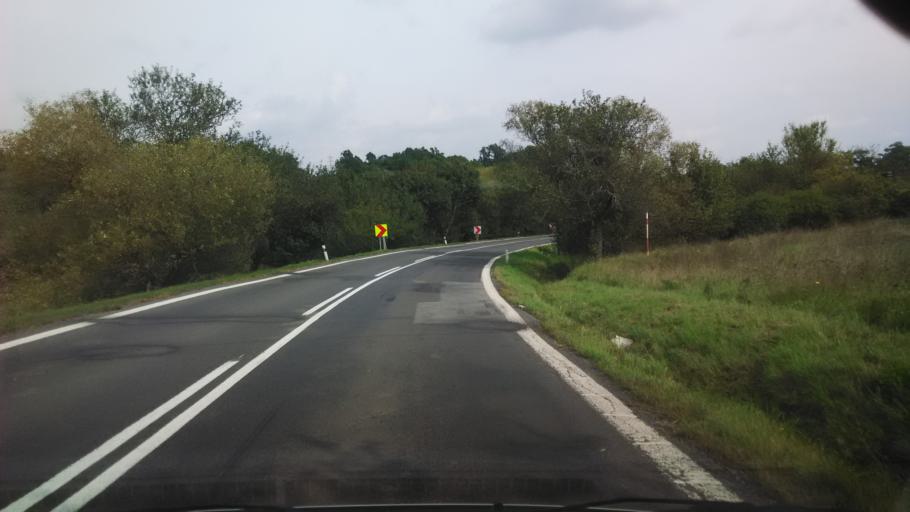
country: SK
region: Banskobystricky
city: Krupina
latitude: 48.3130
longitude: 19.0333
